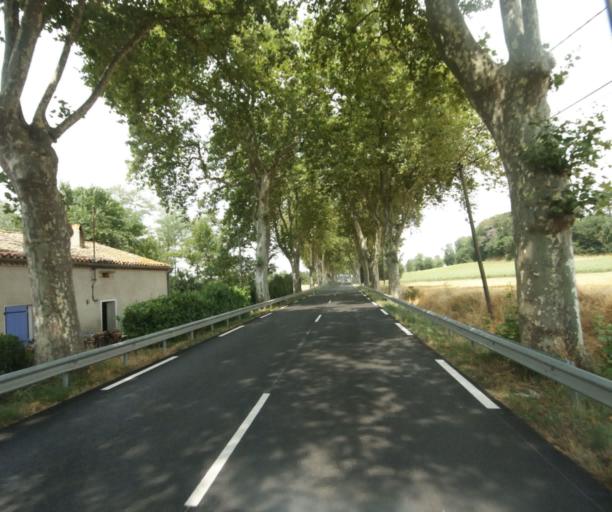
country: FR
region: Midi-Pyrenees
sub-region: Departement de la Haute-Garonne
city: Revel
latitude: 43.4412
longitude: 1.9520
